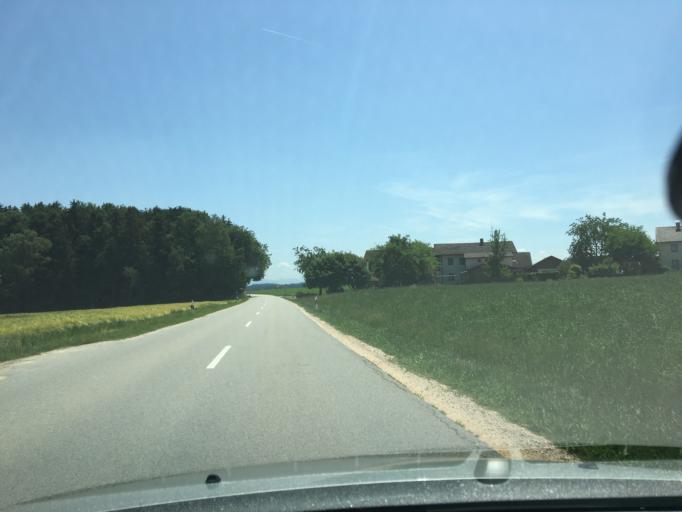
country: DE
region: Bavaria
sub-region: Upper Bavaria
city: Halsbach
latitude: 48.1303
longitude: 12.6644
